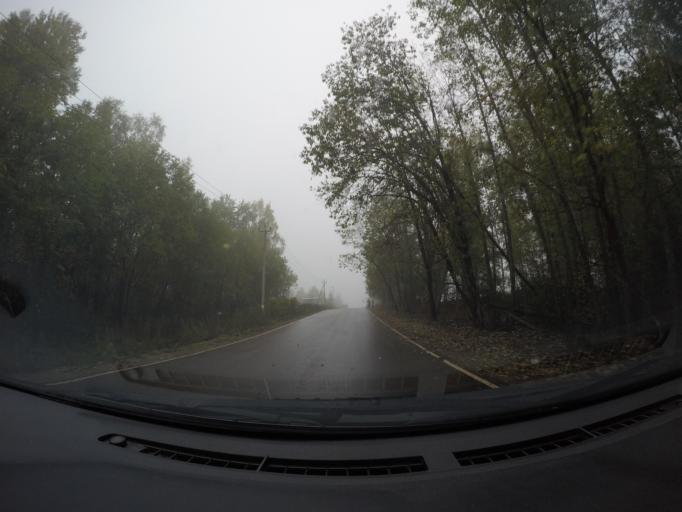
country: RU
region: Moskovskaya
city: Ruza
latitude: 55.7896
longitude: 36.2494
